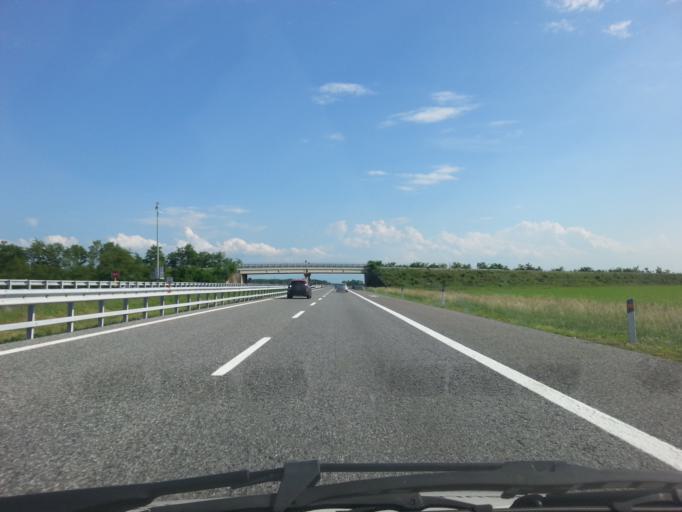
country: IT
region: Piedmont
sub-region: Provincia di Cuneo
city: Sommariva del Bosco
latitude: 44.7370
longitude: 7.7535
